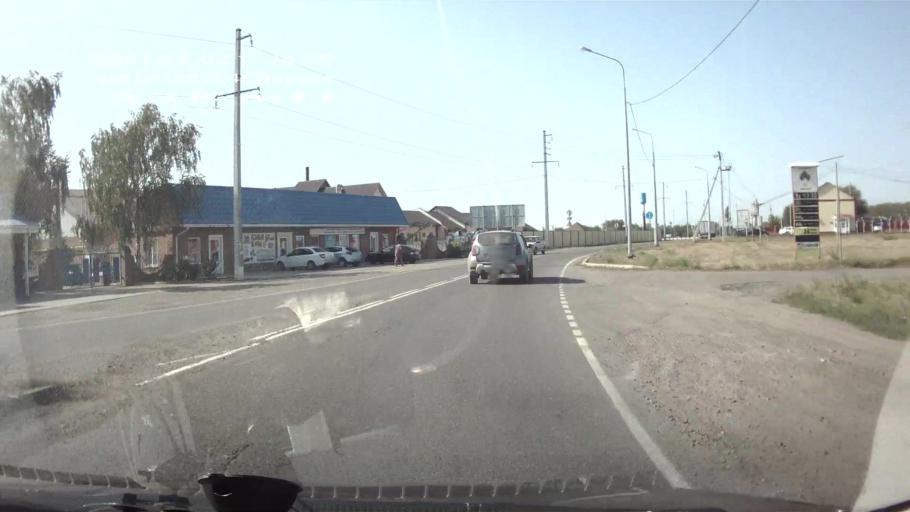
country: RU
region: Krasnodarskiy
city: Belaya Glina
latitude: 46.0936
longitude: 40.8424
